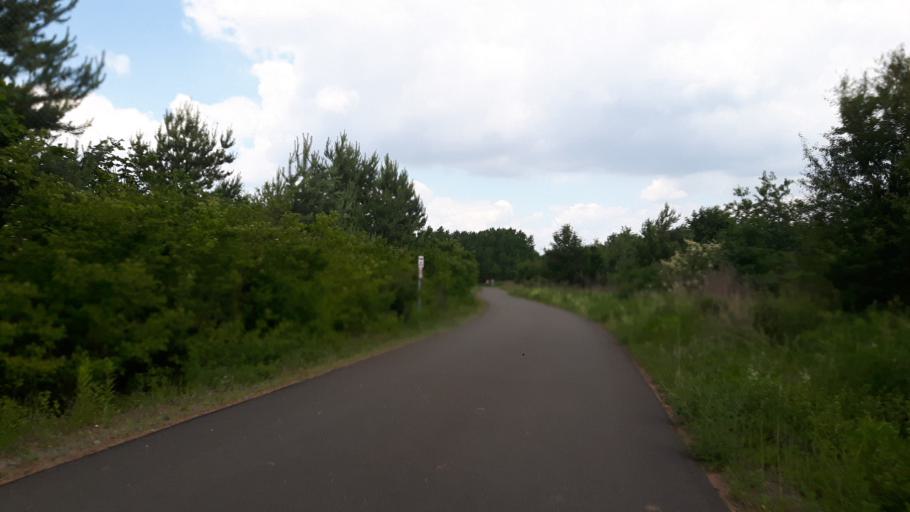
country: DE
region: Saxony-Anhalt
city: Grafenhainichen
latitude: 51.7083
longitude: 12.4640
